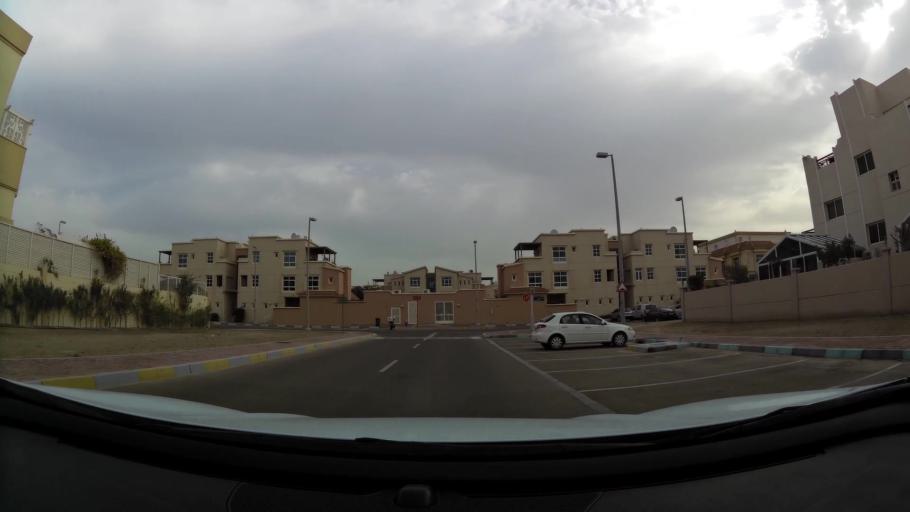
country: AE
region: Abu Dhabi
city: Abu Dhabi
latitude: 24.4727
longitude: 54.3842
